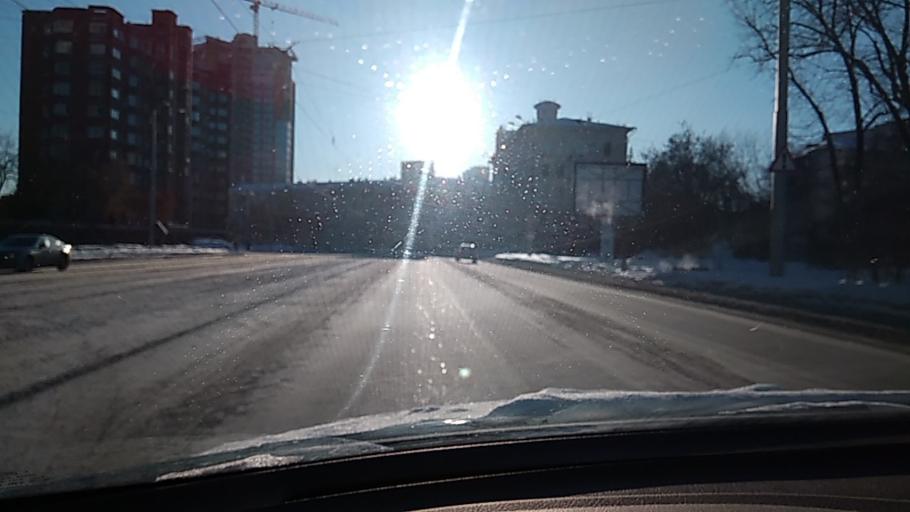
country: RU
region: Sverdlovsk
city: Yekaterinburg
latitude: 56.8422
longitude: 60.5820
